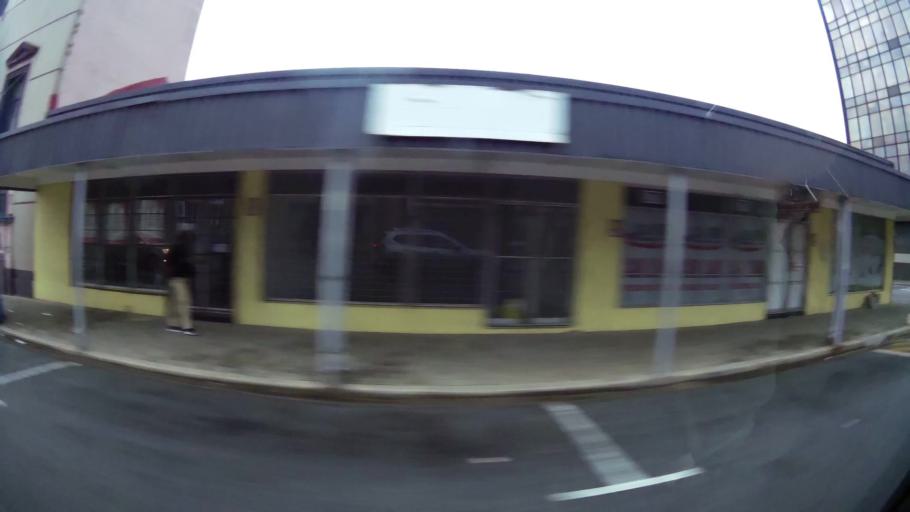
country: ZA
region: Eastern Cape
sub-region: Nelson Mandela Bay Metropolitan Municipality
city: Port Elizabeth
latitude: -33.9449
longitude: 25.6062
